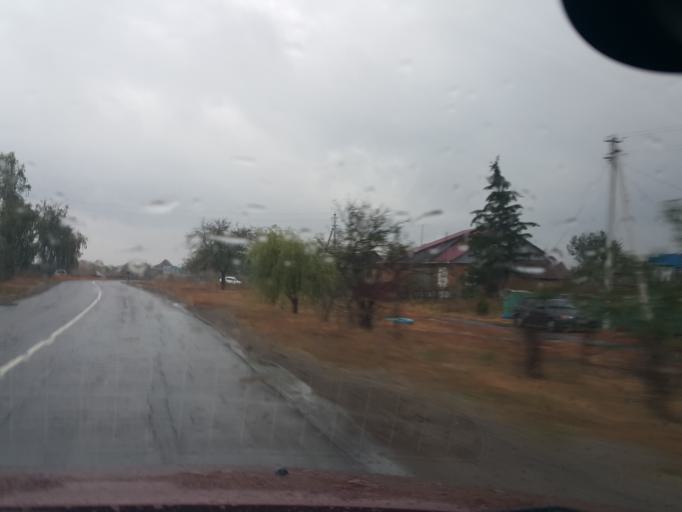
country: RU
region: Tambov
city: Kotovsk
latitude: 52.5367
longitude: 41.4766
